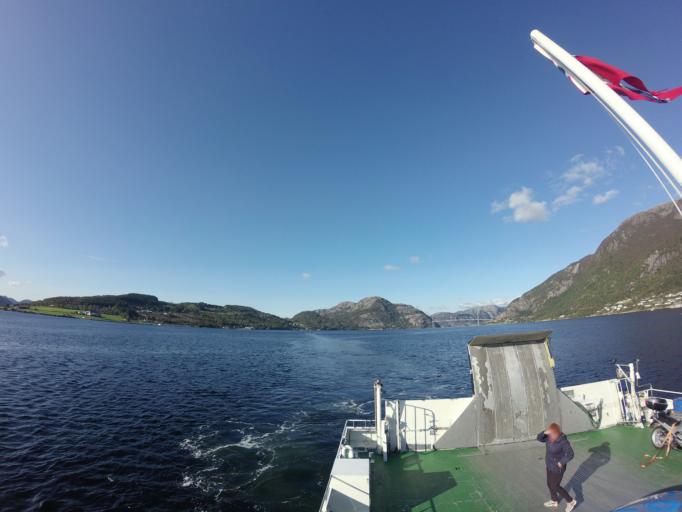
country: NO
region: Rogaland
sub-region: Forsand
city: Forsand
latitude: 58.9018
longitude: 6.0877
